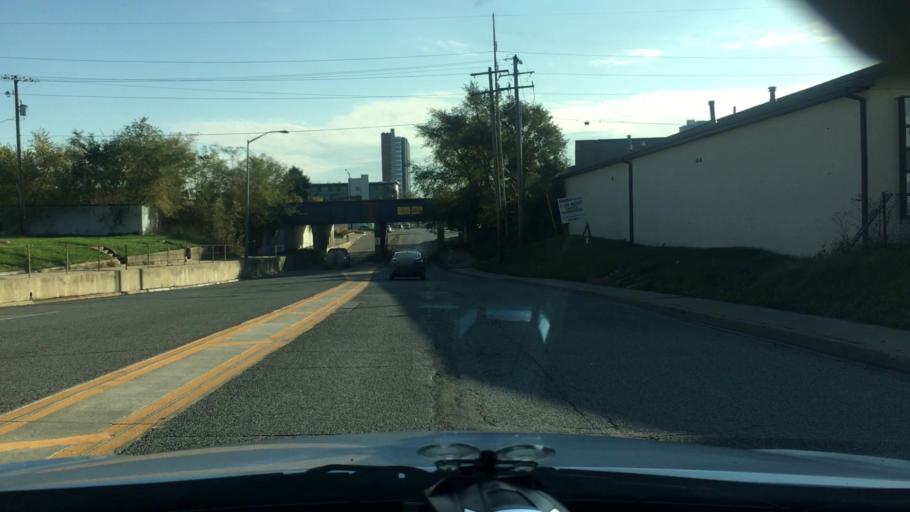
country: US
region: Illinois
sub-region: Champaign County
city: Champaign
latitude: 40.1126
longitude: -88.2429
